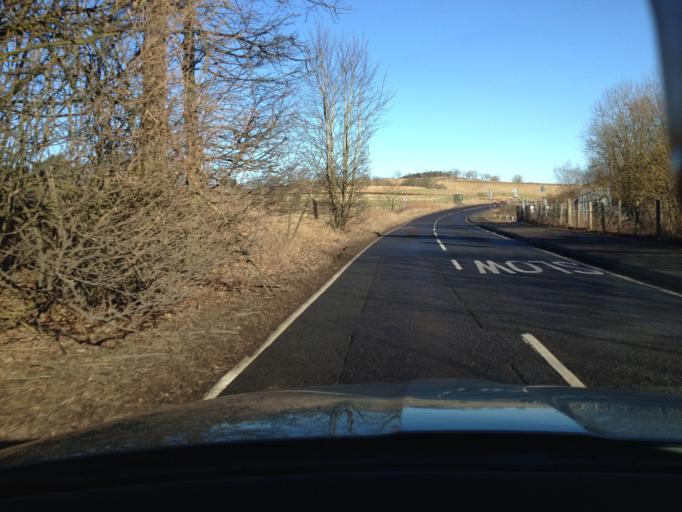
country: GB
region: Scotland
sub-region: Perth and Kinross
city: Bridge of Earn
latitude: 56.2864
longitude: -3.3958
